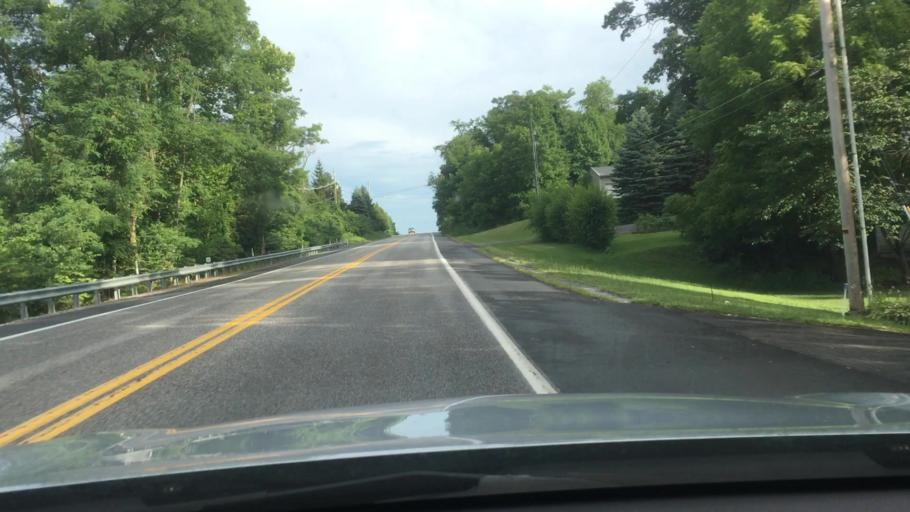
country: US
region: Pennsylvania
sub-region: York County
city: Dover
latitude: 40.0759
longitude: -76.9261
